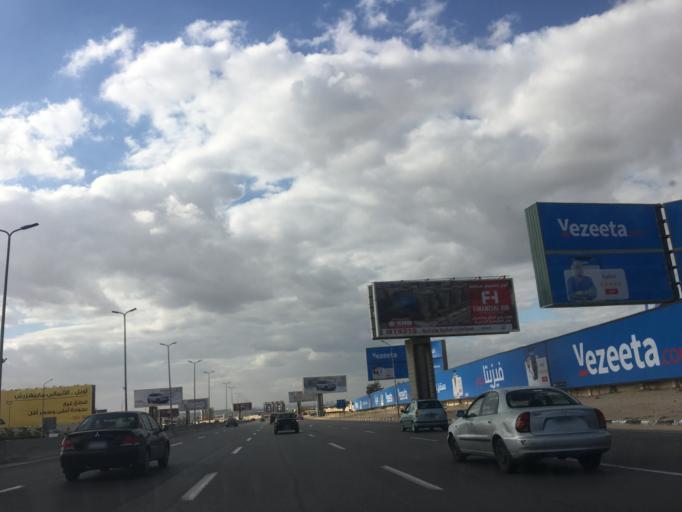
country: EG
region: Muhafazat al Qahirah
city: Cairo
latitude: 30.0239
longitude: 31.3652
